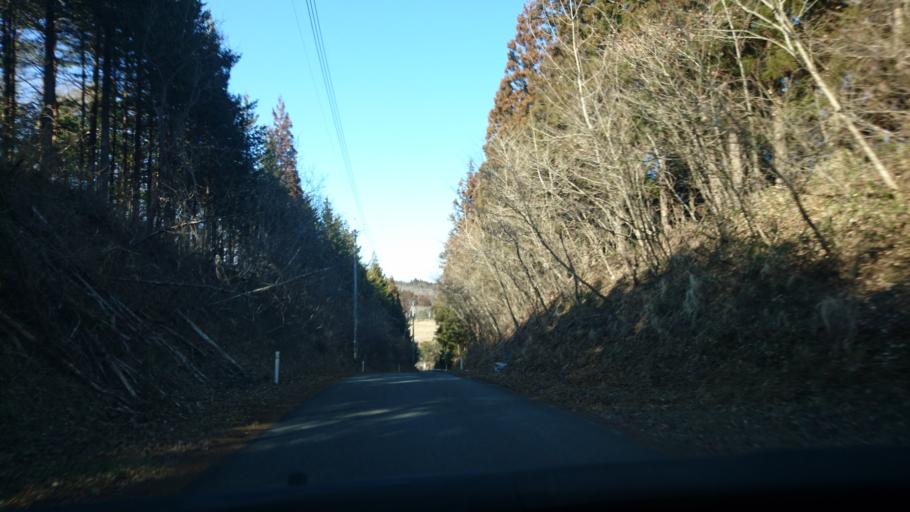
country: JP
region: Iwate
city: Ichinoseki
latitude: 38.8523
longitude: 141.2313
